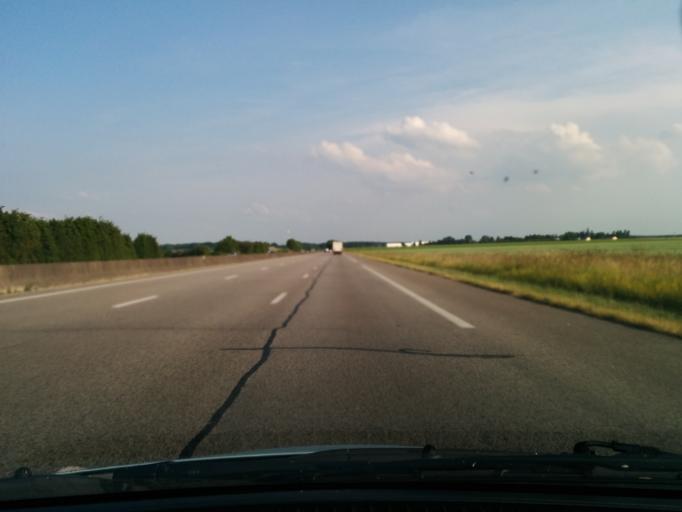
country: FR
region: Haute-Normandie
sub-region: Departement de l'Eure
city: Saint-Aubin-sur-Gaillon
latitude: 49.1196
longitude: 1.3302
